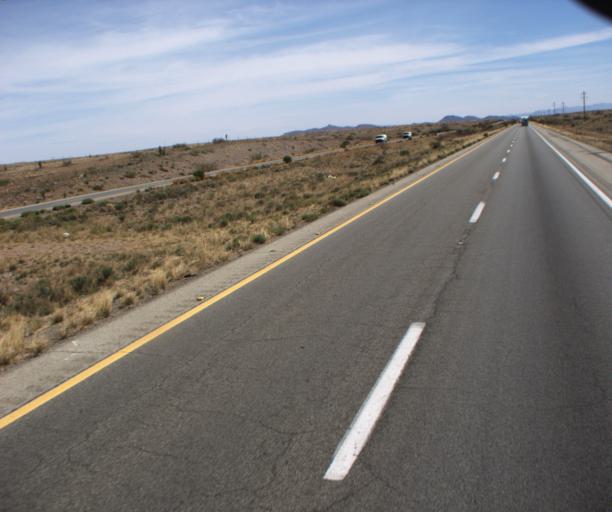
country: US
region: Arizona
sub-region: Cochise County
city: Willcox
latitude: 32.3496
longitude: -109.7370
